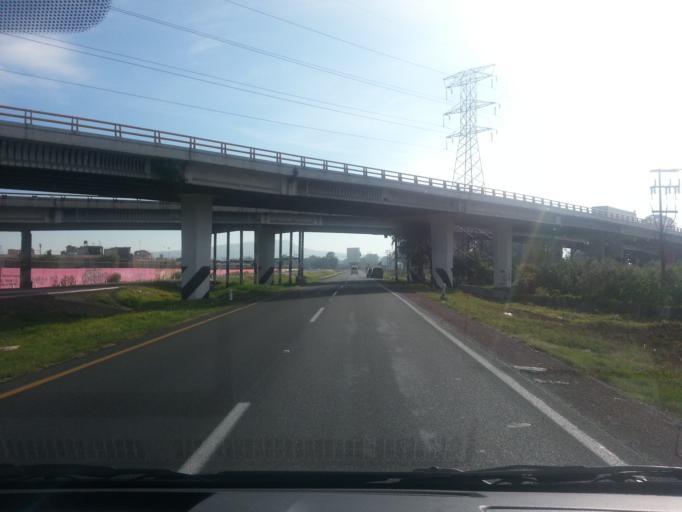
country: MX
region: Mexico
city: Santo Tomas Chiconautla
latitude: 19.6141
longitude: -99.0168
